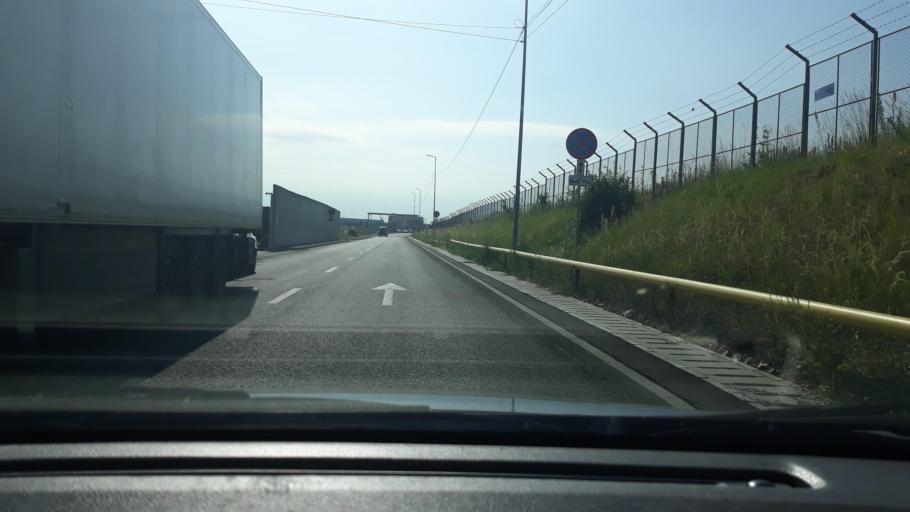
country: RO
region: Bihor
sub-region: Comuna Biharea
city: Oradea
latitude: 47.0399
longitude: 21.9033
